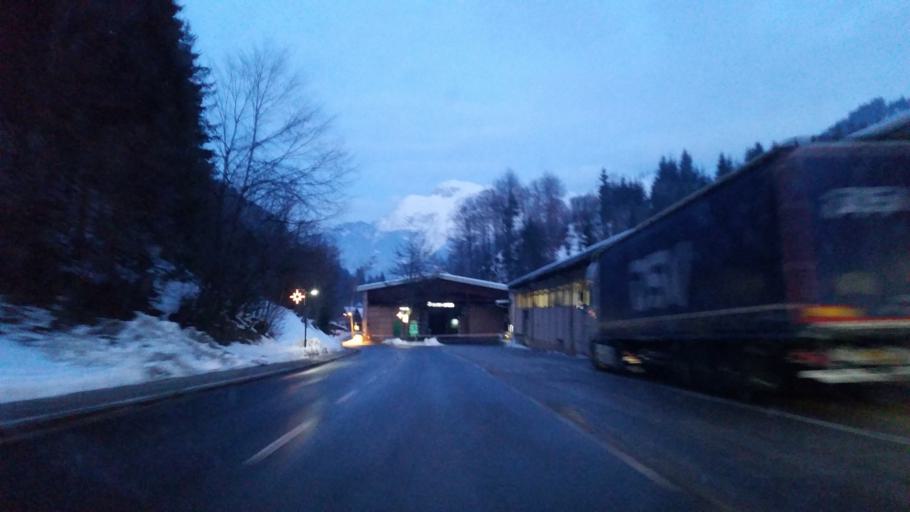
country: AT
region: Salzburg
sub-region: Politischer Bezirk Hallein
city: Abtenau
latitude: 47.4951
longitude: 13.4025
